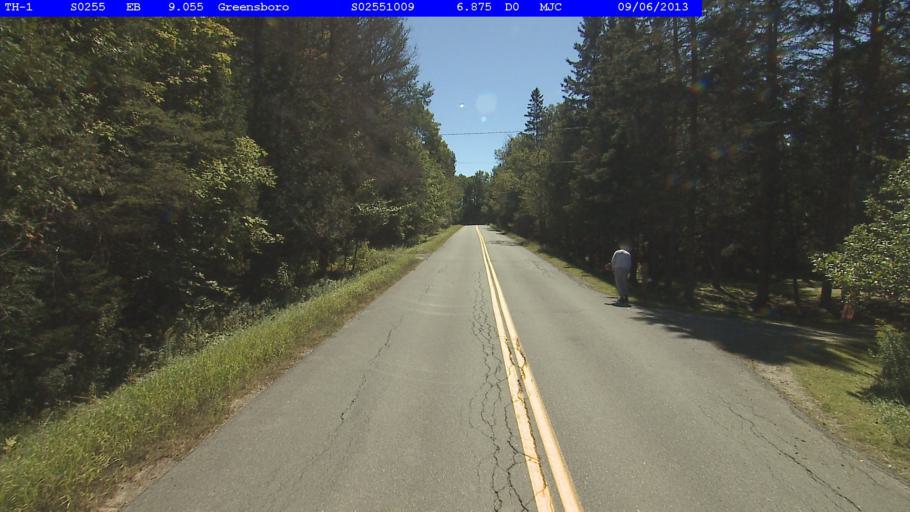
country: US
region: Vermont
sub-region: Caledonia County
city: Hardwick
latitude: 44.5553
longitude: -72.2757
